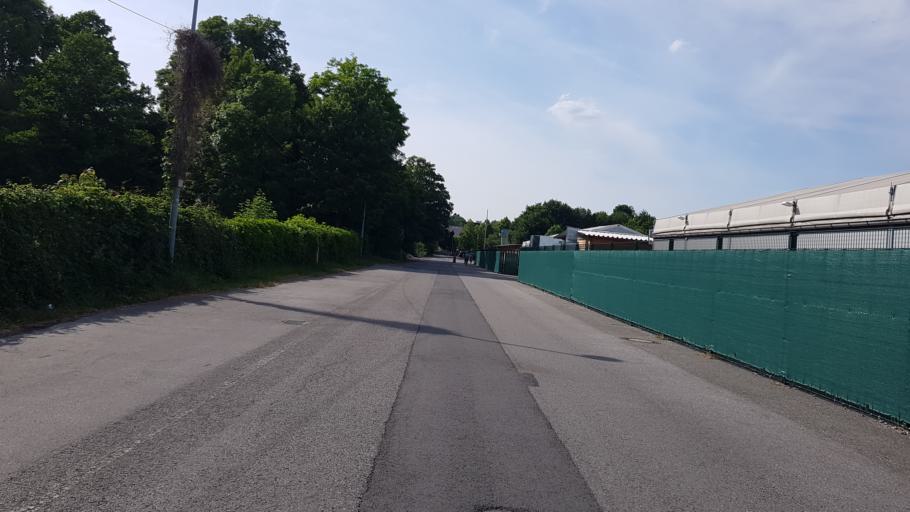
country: DE
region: North Rhine-Westphalia
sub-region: Regierungsbezirk Dusseldorf
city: Muelheim (Ruhr)
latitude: 51.4088
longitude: 6.8744
